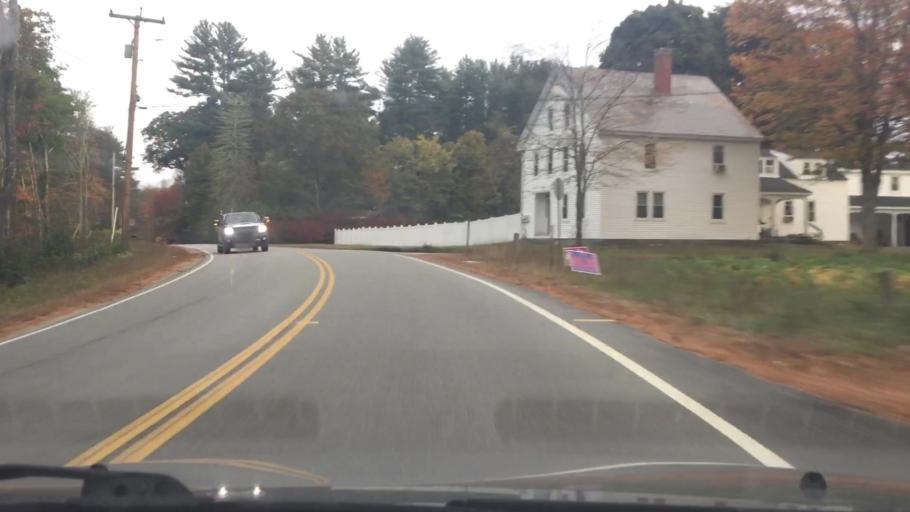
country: US
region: New Hampshire
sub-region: Cheshire County
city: Swanzey
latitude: 42.8443
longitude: -72.2789
